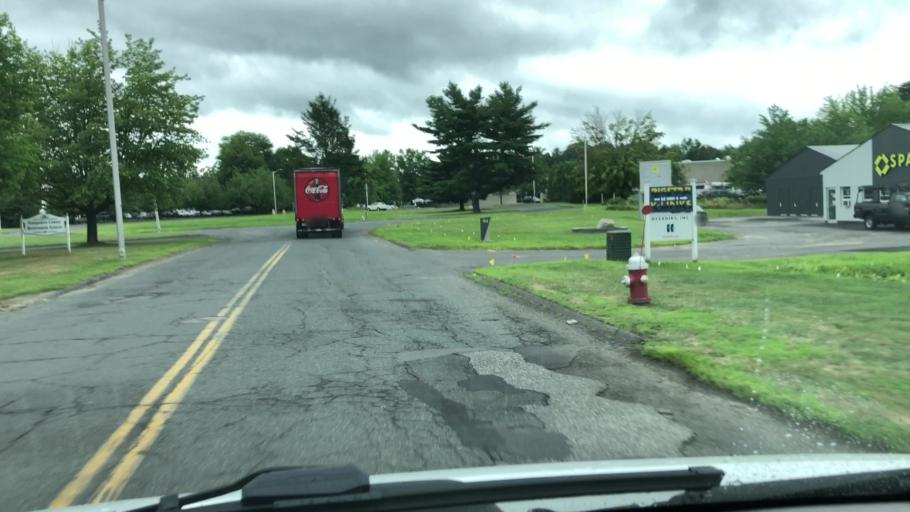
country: US
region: Massachusetts
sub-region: Hampshire County
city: Northampton
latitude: 42.3350
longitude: -72.6307
